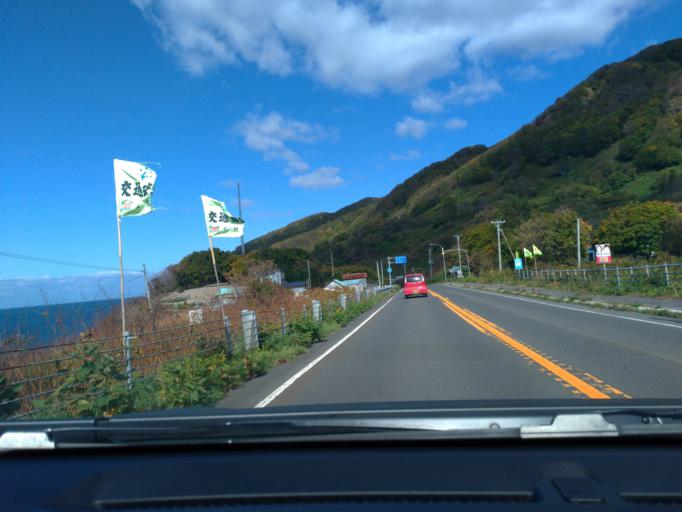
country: JP
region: Hokkaido
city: Ishikari
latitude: 43.4186
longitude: 141.4295
